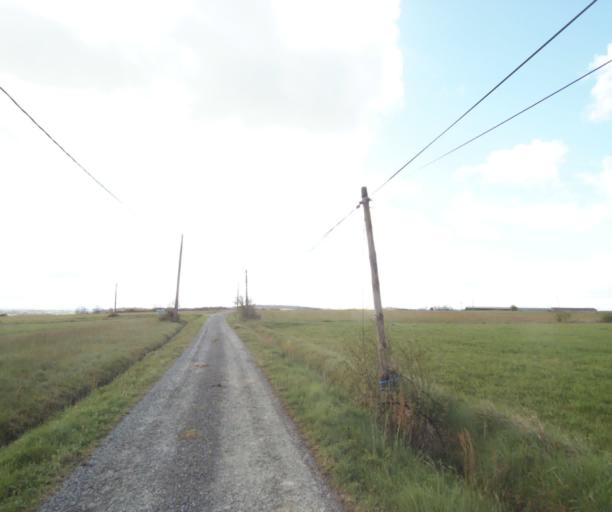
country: FR
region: Midi-Pyrenees
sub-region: Departement de l'Ariege
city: Saverdun
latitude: 43.2320
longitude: 1.5332
